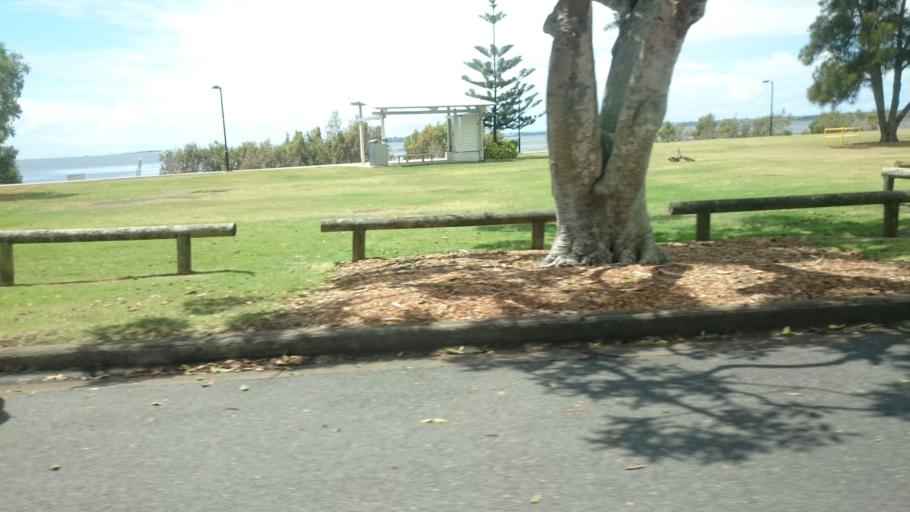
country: AU
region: Queensland
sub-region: Brisbane
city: Manly West
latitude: -27.4653
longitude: 153.1919
